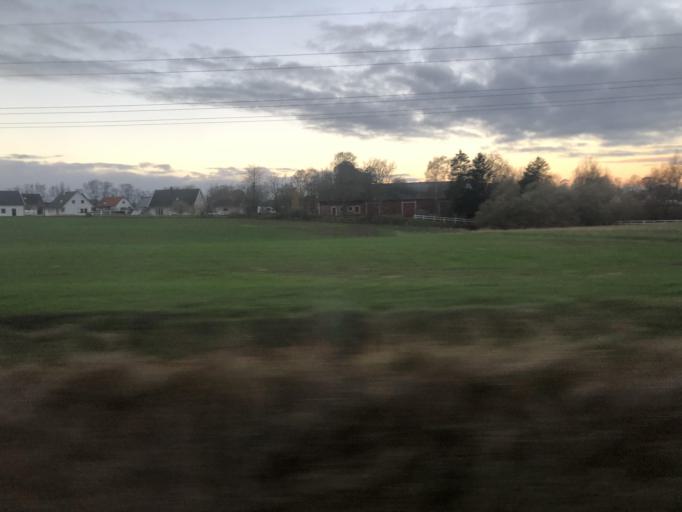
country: SE
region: Skane
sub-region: Kavlinge Kommun
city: Kaevlinge
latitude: 55.7748
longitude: 13.1173
